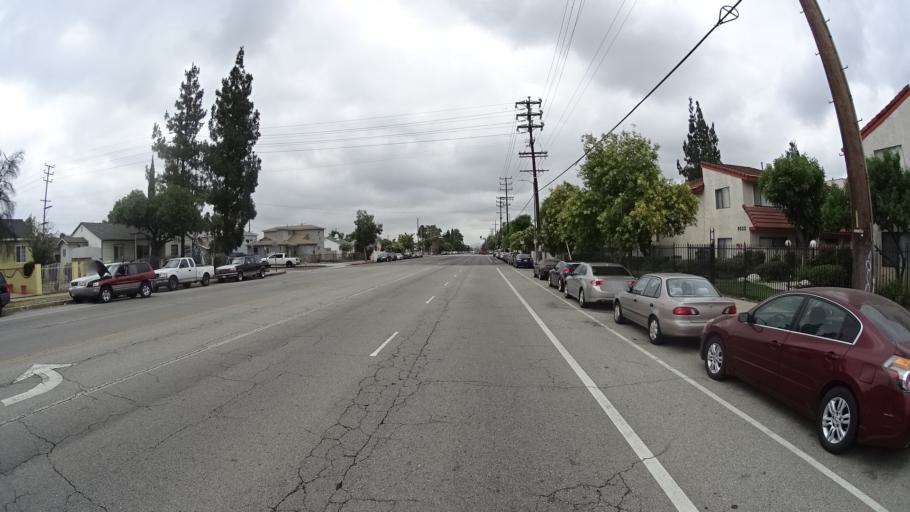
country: US
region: California
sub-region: Los Angeles County
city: San Fernando
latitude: 34.2439
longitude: -118.4463
